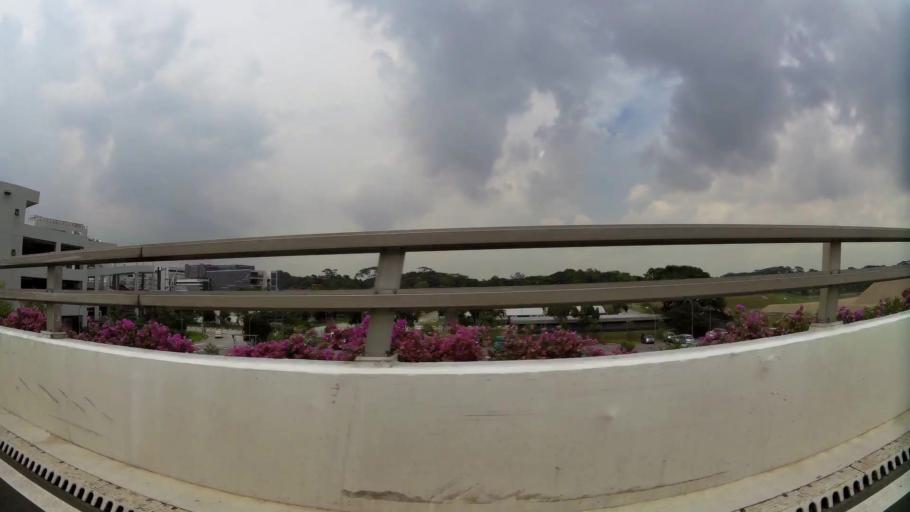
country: SG
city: Singapore
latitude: 1.3421
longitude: 103.9156
